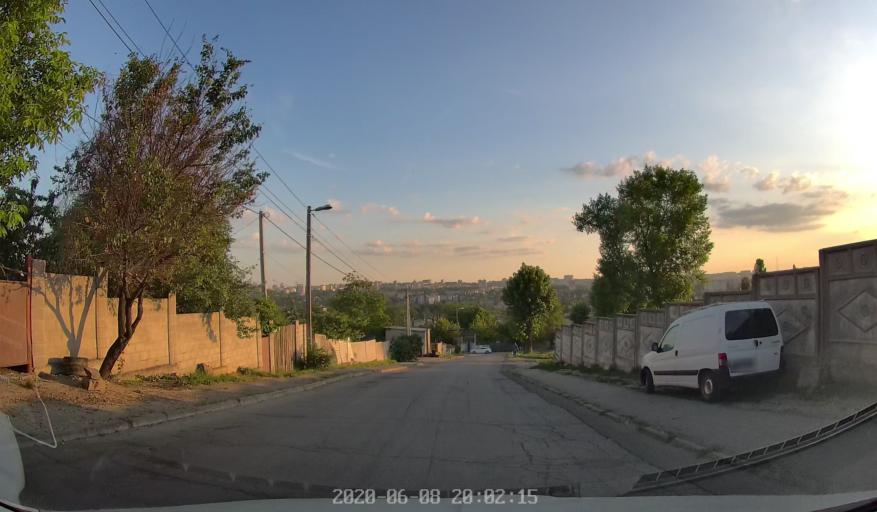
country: MD
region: Chisinau
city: Chisinau
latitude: 47.0099
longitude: 28.8848
